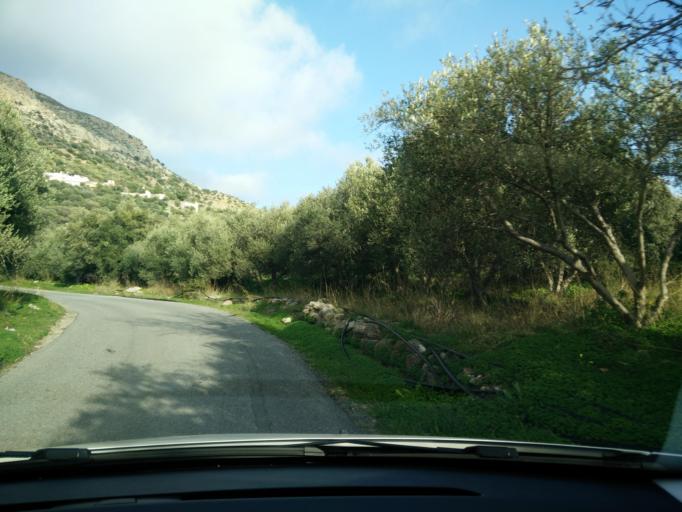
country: GR
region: Crete
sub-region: Nomos Lasithiou
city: Gra Liyia
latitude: 35.0262
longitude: 25.5460
